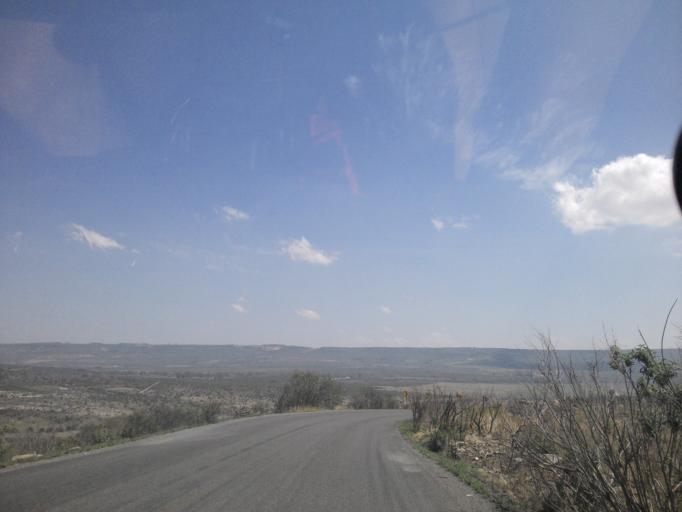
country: MX
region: Jalisco
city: San Diego de Alejandria
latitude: 20.8702
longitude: -102.0813
